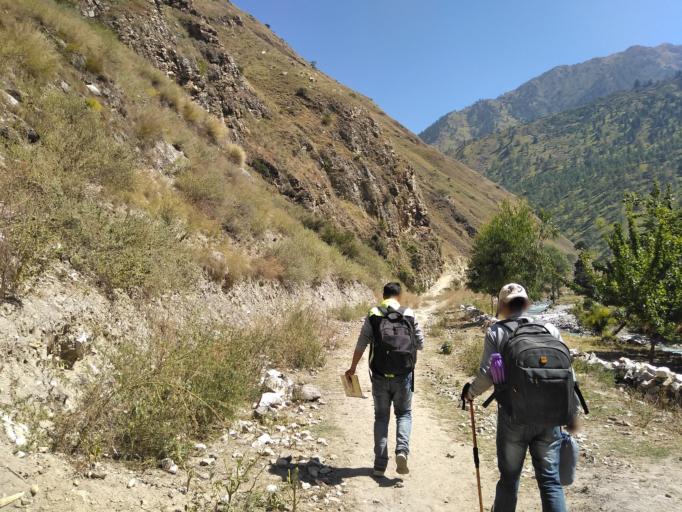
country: NP
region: Mid Western
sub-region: Karnali Zone
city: Jumla
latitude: 28.9353
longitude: 82.9088
